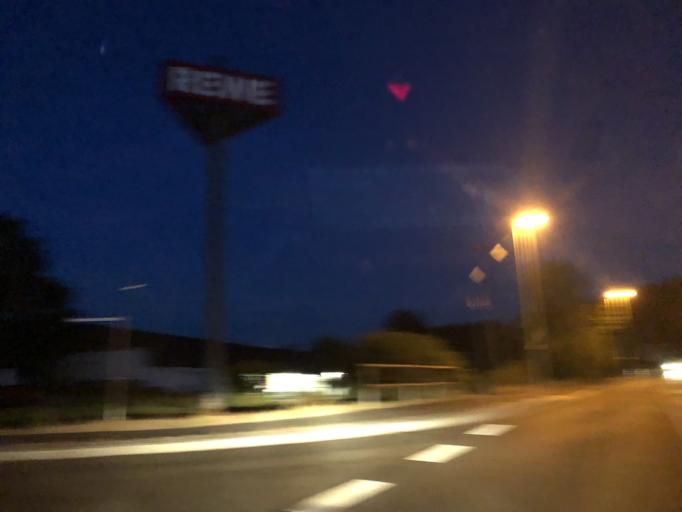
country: DE
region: Bavaria
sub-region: Upper Franconia
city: Hirschaid
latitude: 49.8061
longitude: 10.9697
